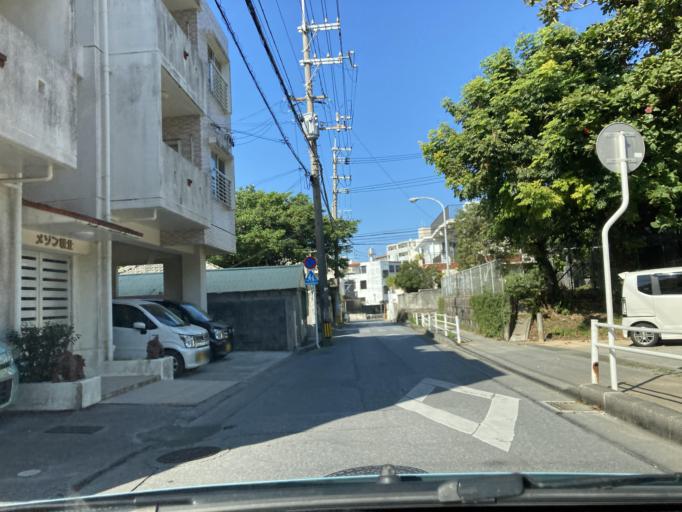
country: JP
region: Okinawa
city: Naha-shi
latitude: 26.2268
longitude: 127.7214
